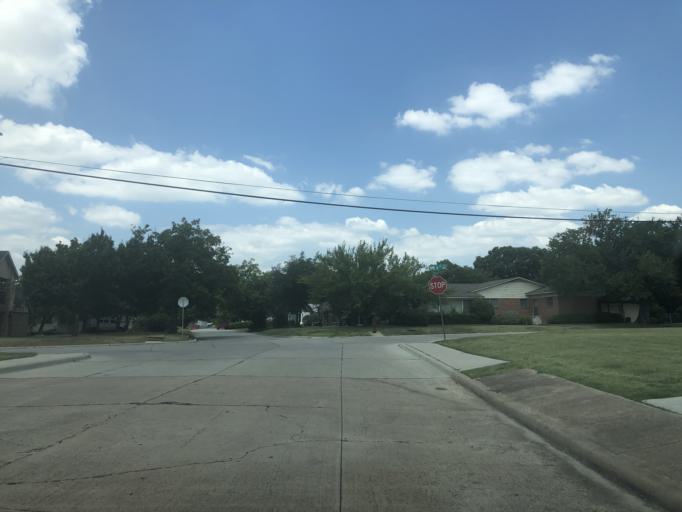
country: US
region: Texas
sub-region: Dallas County
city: Grand Prairie
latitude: 32.7466
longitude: -97.0100
